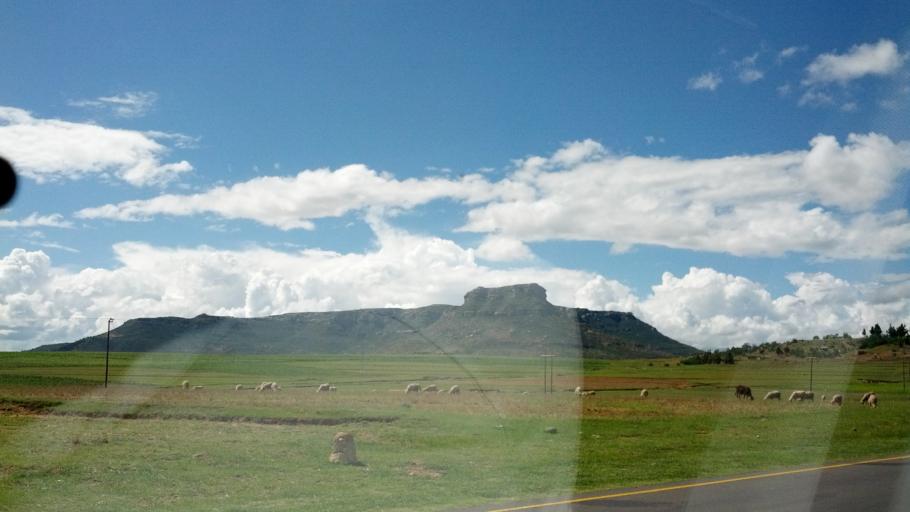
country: LS
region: Mafeteng
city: Mafeteng
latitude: -29.6514
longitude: 27.4596
